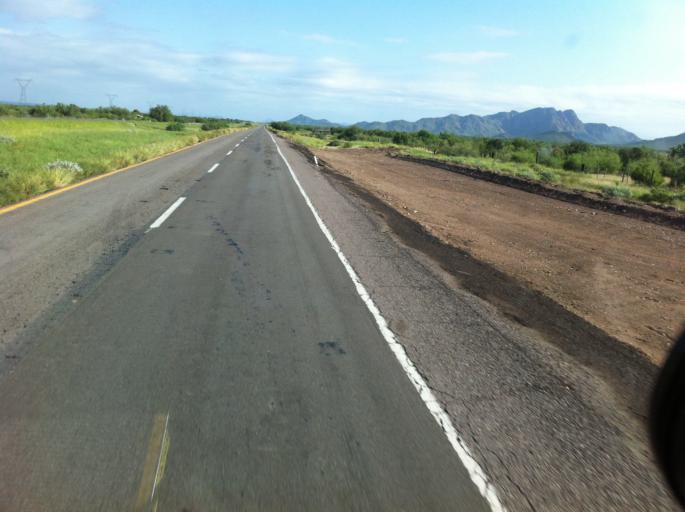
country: MX
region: Sonora
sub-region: Hermosillo
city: Miguel Aleman (La Doce)
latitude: 28.5434
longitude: -111.0413
